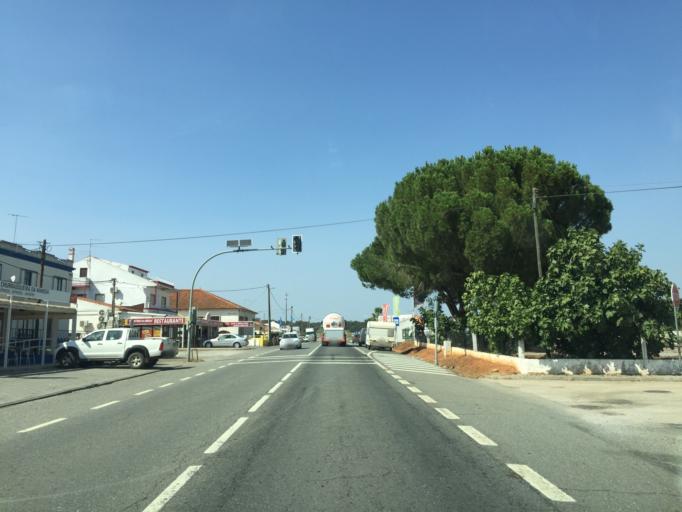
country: PT
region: Beja
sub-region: Aljustrel
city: Aljustrel
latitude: 37.9467
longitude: -8.3807
